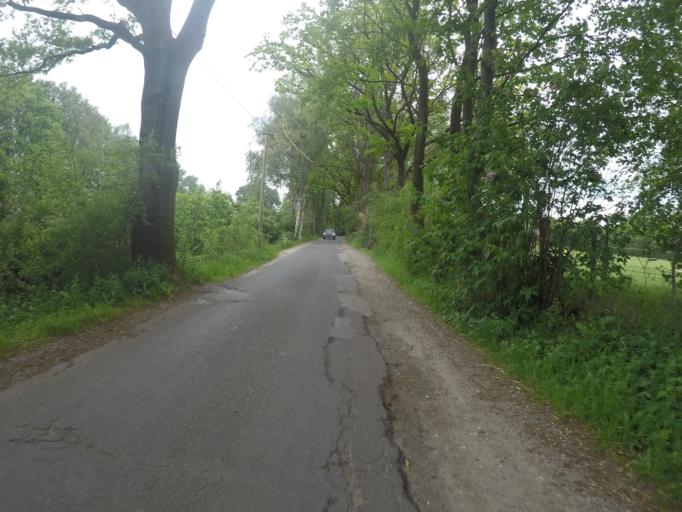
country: DE
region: Schleswig-Holstein
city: Bonningstedt
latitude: 53.6537
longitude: 9.9399
